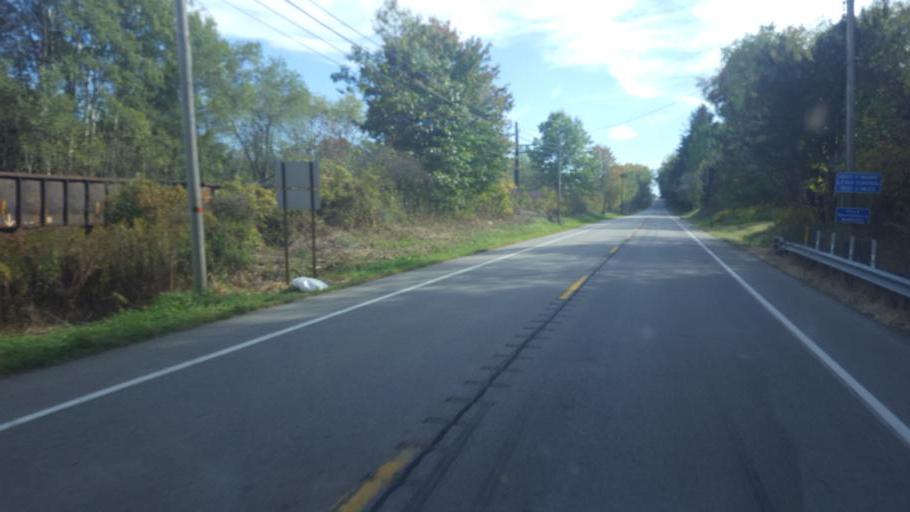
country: US
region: Pennsylvania
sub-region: Mercer County
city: Mercer
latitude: 41.2890
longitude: -80.2396
